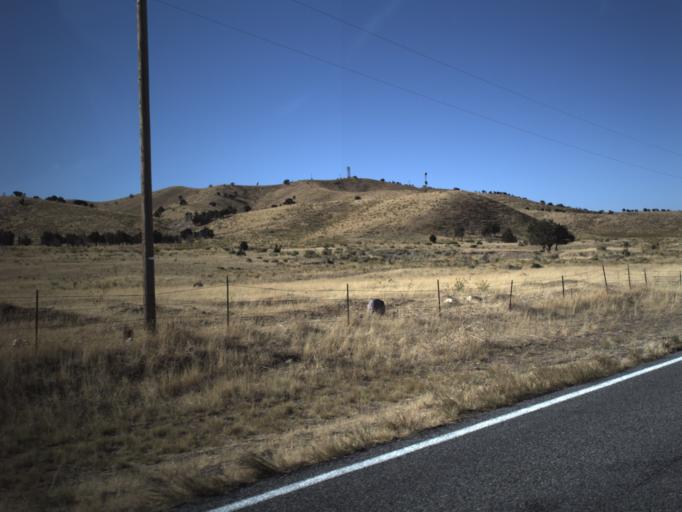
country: US
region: Utah
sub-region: Millard County
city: Delta
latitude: 39.3637
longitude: -112.3463
